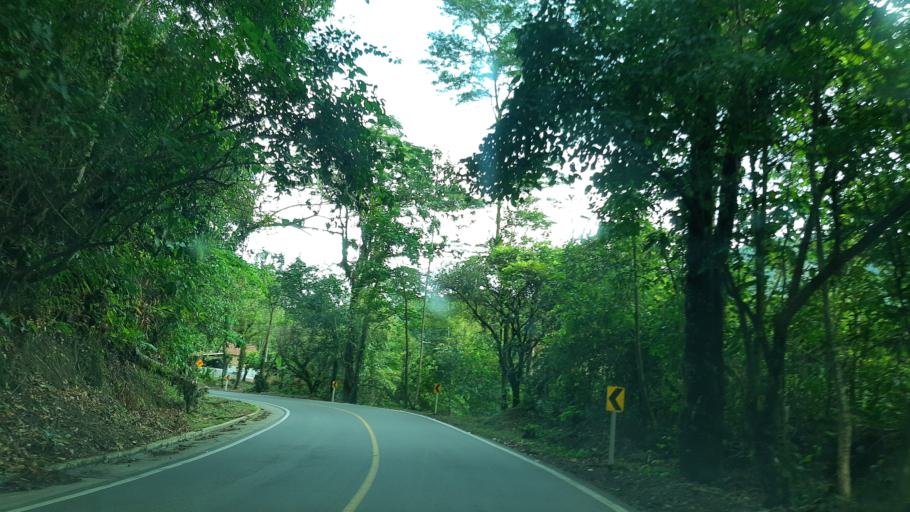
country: CO
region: Boyaca
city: San Luis de Gaceno
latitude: 4.8395
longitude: -73.2149
